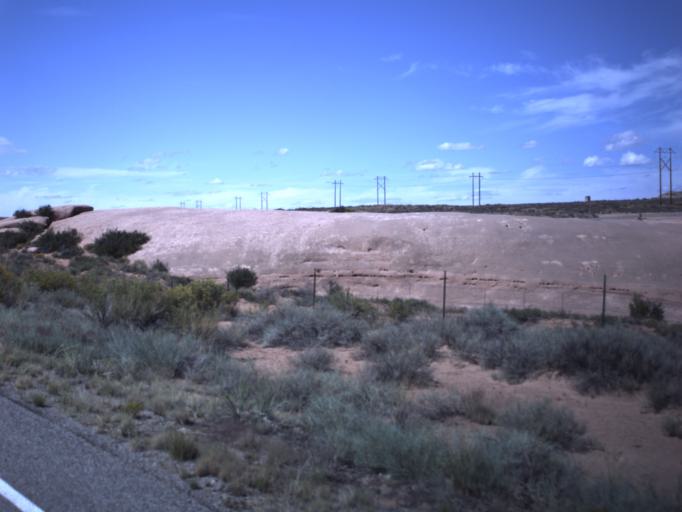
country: US
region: Utah
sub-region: San Juan County
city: Blanding
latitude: 37.2985
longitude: -109.4639
